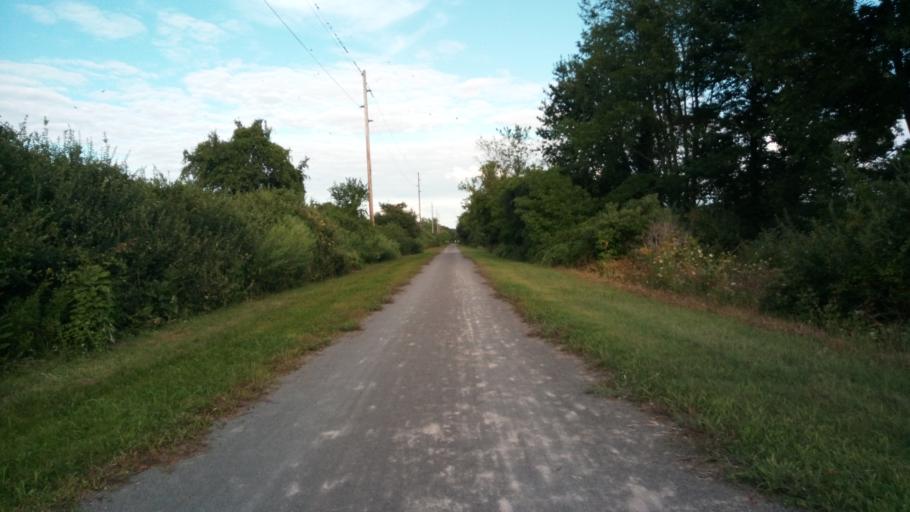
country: US
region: New York
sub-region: Ontario County
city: Victor
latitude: 43.0022
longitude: -77.4748
